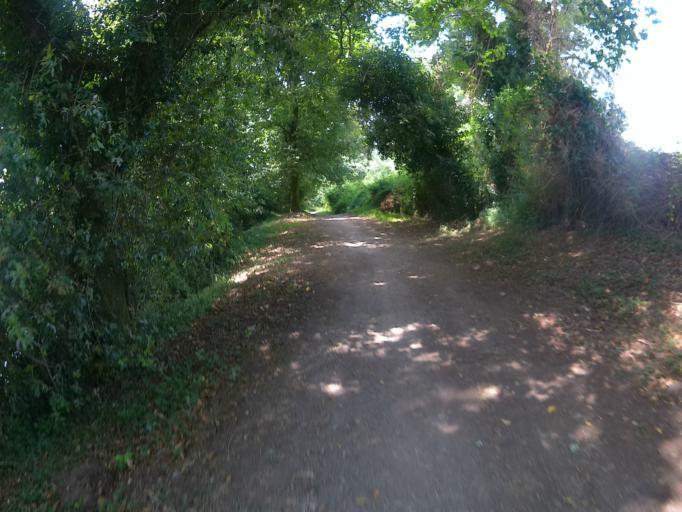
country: PT
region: Viana do Castelo
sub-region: Ponte de Lima
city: Ponte de Lima
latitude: 41.7769
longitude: -8.5832
